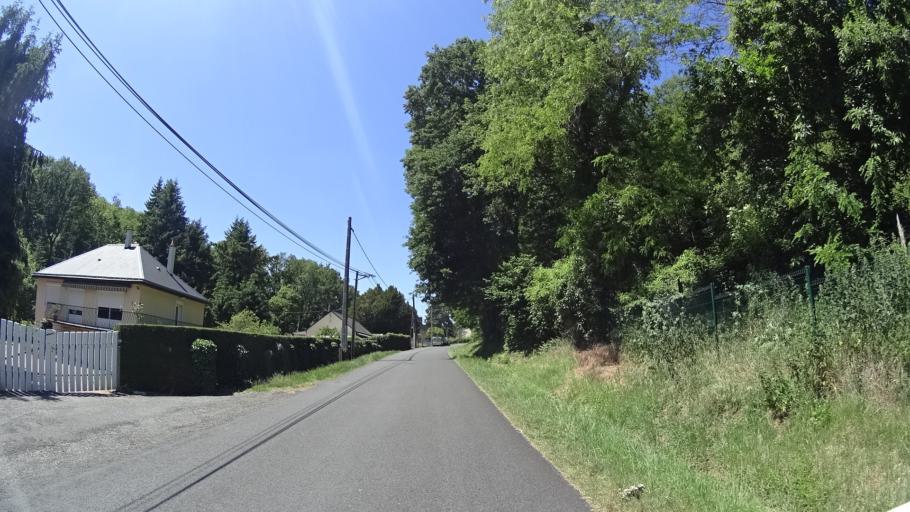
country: FR
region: Pays de la Loire
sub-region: Departement de Maine-et-Loire
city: Saumur
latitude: 47.2794
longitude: -0.1232
